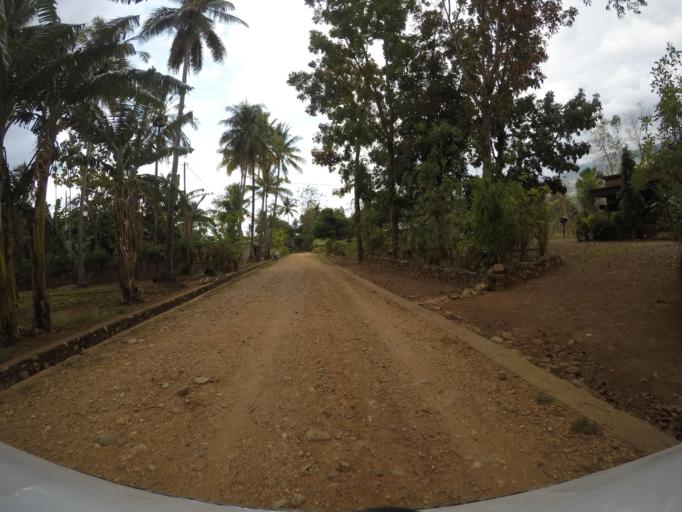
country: TL
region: Bobonaro
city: Maliana
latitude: -8.9638
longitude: 125.2176
